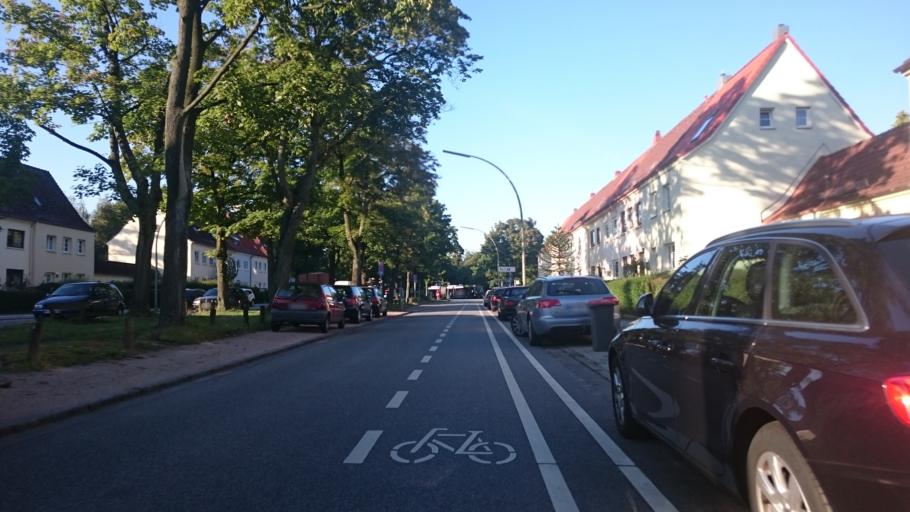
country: DE
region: Hamburg
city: Eidelstedt
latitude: 53.5723
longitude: 9.8912
